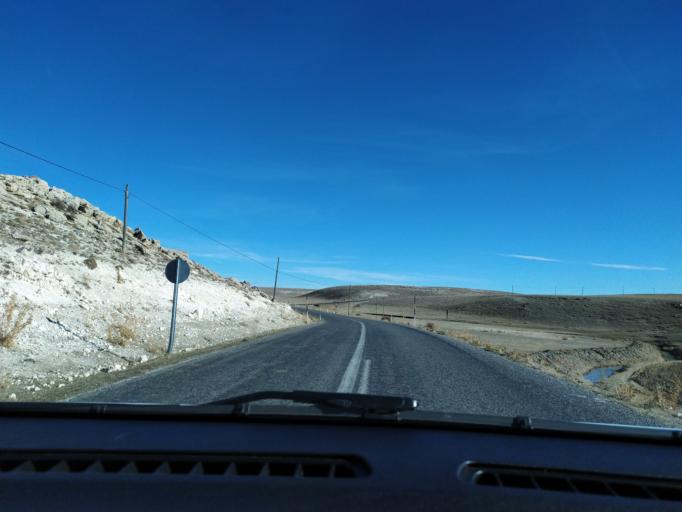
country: TR
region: Kayseri
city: Orensehir
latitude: 38.9779
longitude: 36.6695
